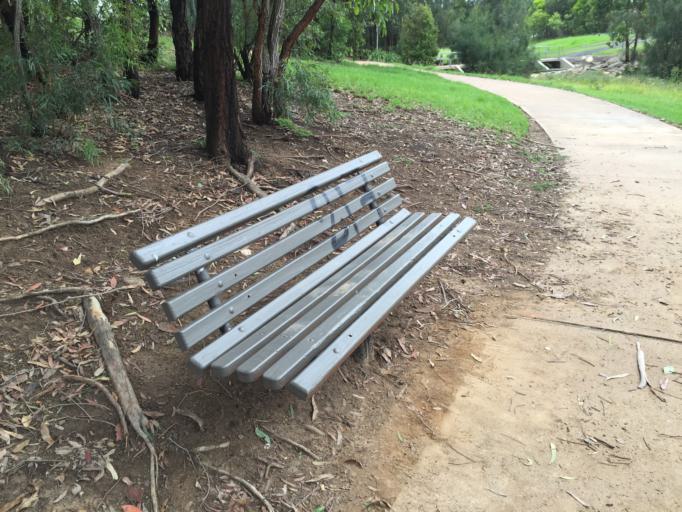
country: AU
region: New South Wales
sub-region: Blacktown
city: Blacktown
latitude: -33.7915
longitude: 150.9131
